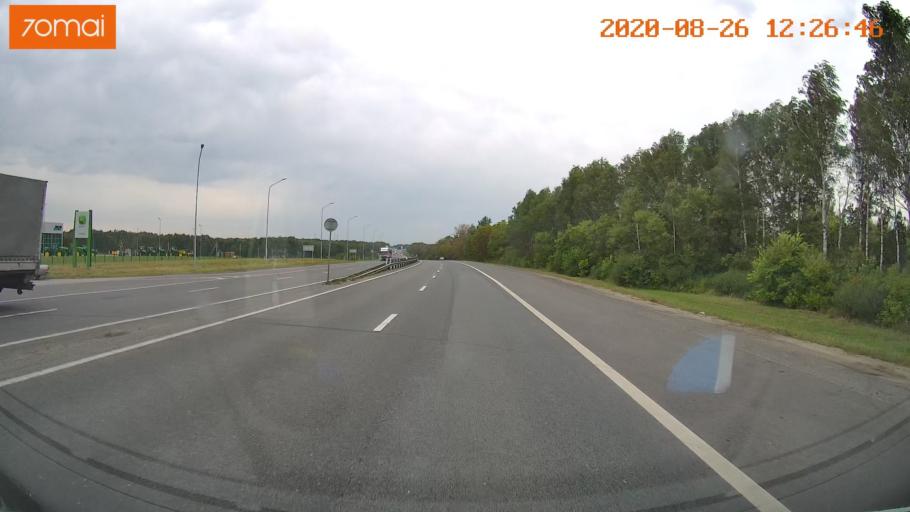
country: RU
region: Rjazan
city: Polyany
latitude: 54.5374
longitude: 39.8532
